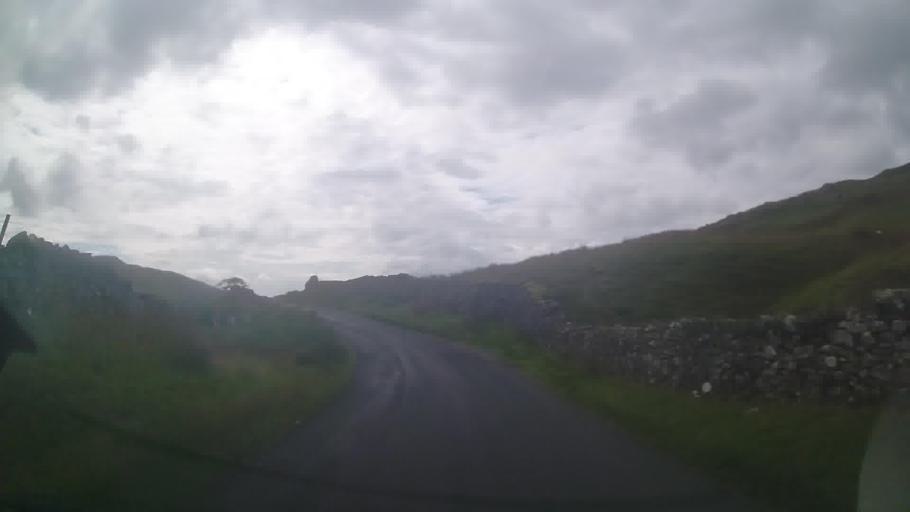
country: GB
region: England
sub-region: Cumbria
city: Ambleside
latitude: 54.4505
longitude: -2.9386
